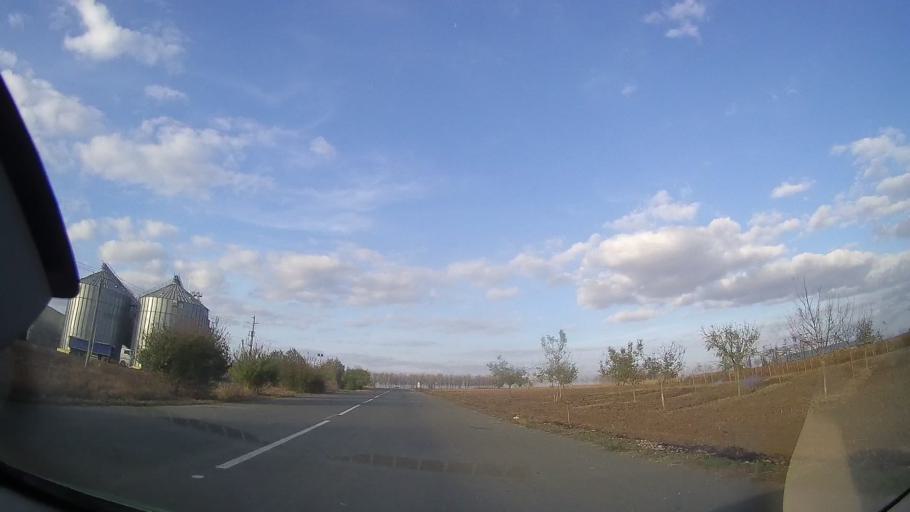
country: RO
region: Constanta
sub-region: Comuna Dumbraveni
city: Dumbraveni
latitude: 43.9260
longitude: 28.0297
